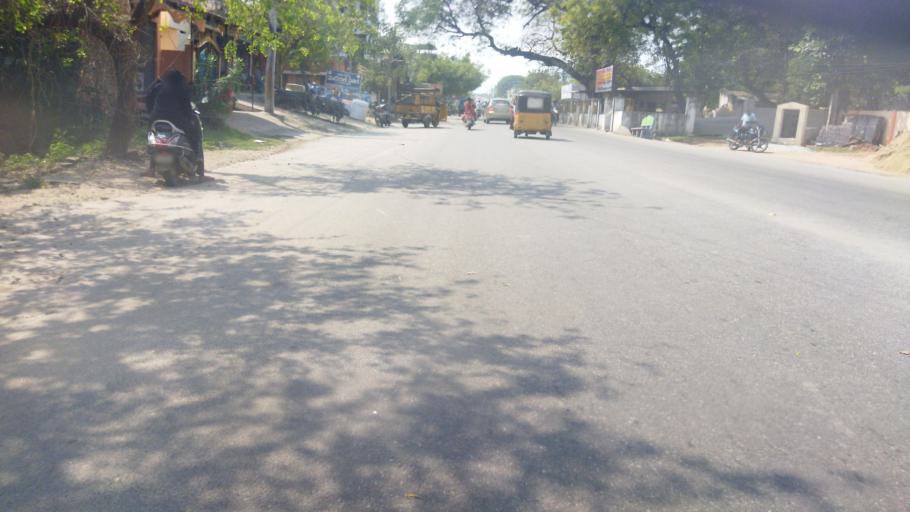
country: IN
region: Telangana
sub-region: Nalgonda
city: Nalgonda
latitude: 17.0697
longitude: 79.2829
